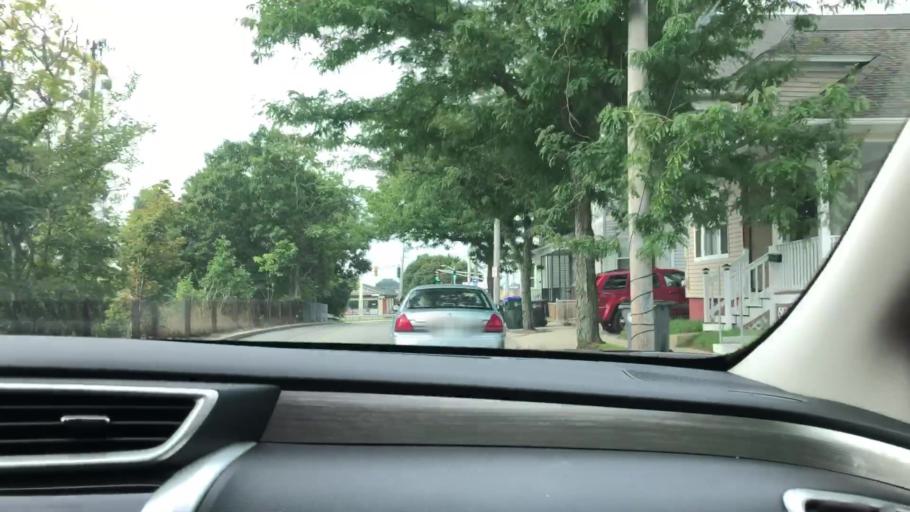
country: US
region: Rhode Island
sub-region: Providence County
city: Providence
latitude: 41.8487
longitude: -71.4143
